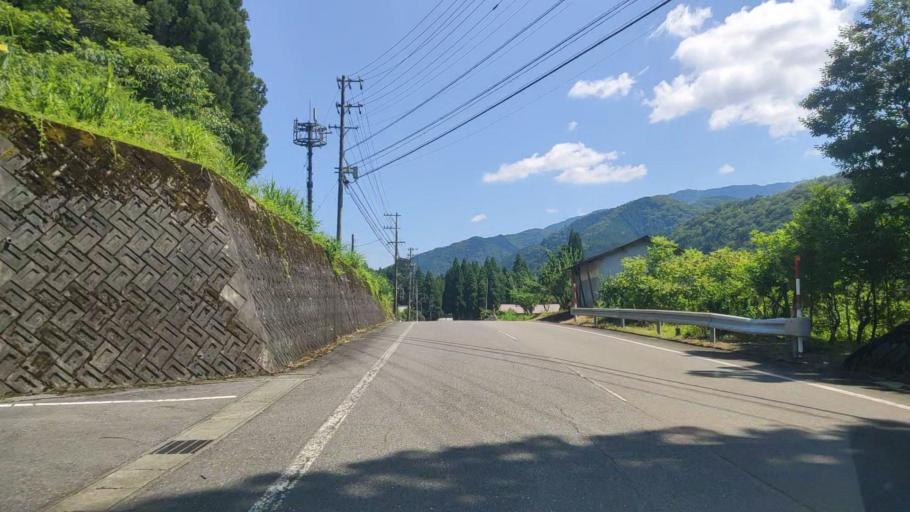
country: JP
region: Gifu
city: Godo
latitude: 35.6673
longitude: 136.5775
